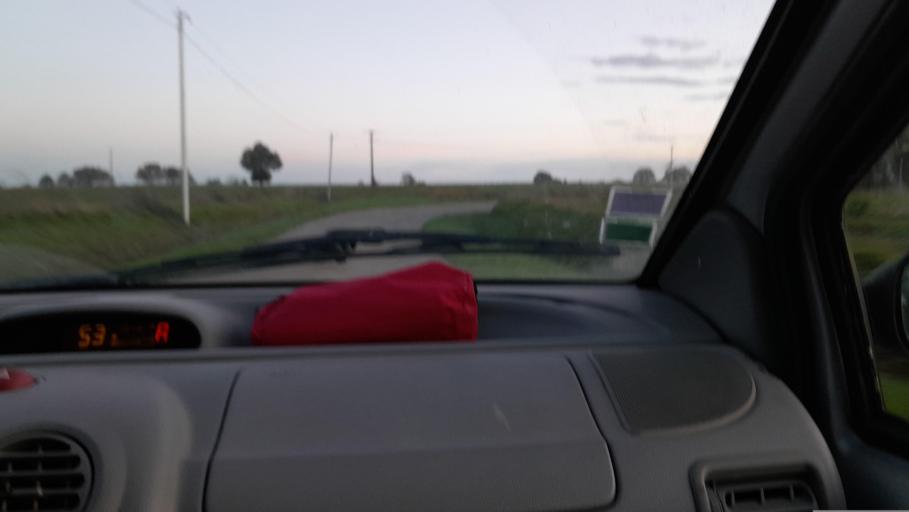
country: FR
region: Brittany
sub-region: Departement d'Ille-et-Vilaine
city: Rannee
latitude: 47.8772
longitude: -1.1838
